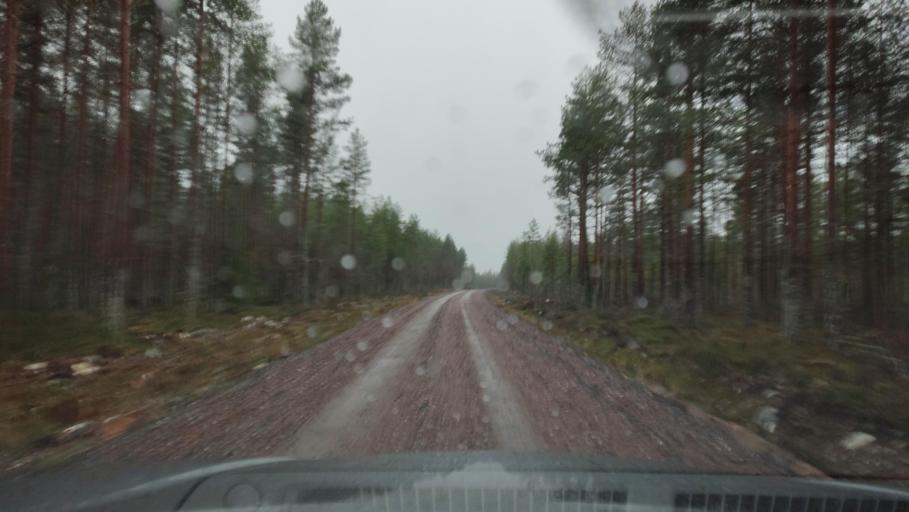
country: FI
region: Southern Ostrobothnia
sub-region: Suupohja
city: Karijoki
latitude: 62.1755
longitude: 21.7104
